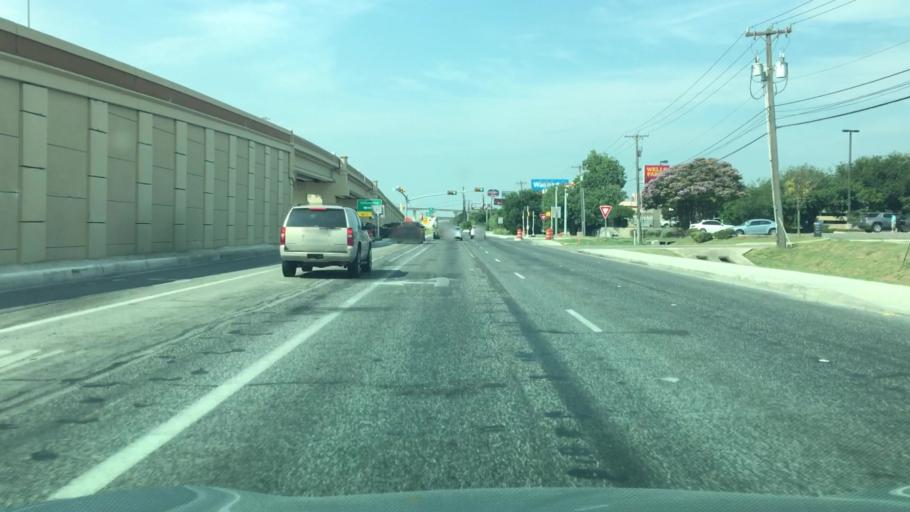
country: US
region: Texas
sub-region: Bexar County
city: Leon Valley
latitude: 29.4436
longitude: -98.6385
